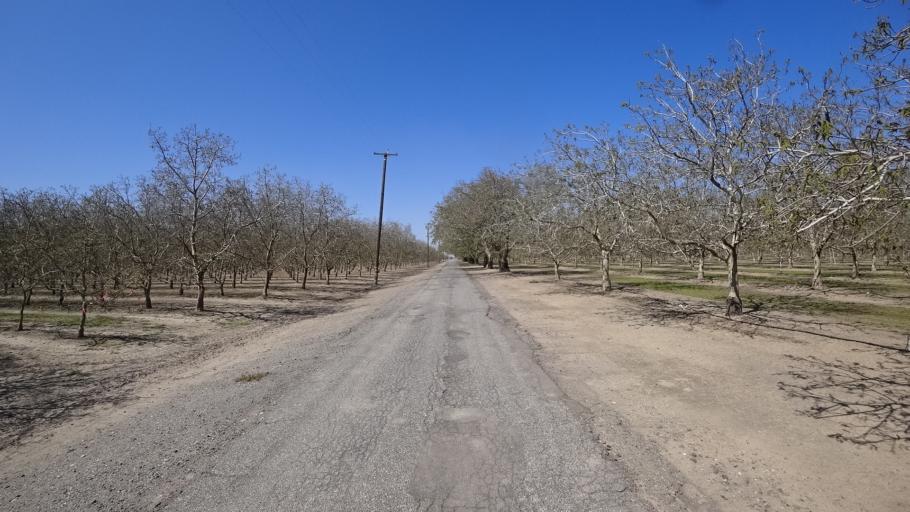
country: US
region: California
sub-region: Glenn County
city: Willows
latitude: 39.4990
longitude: -122.0217
